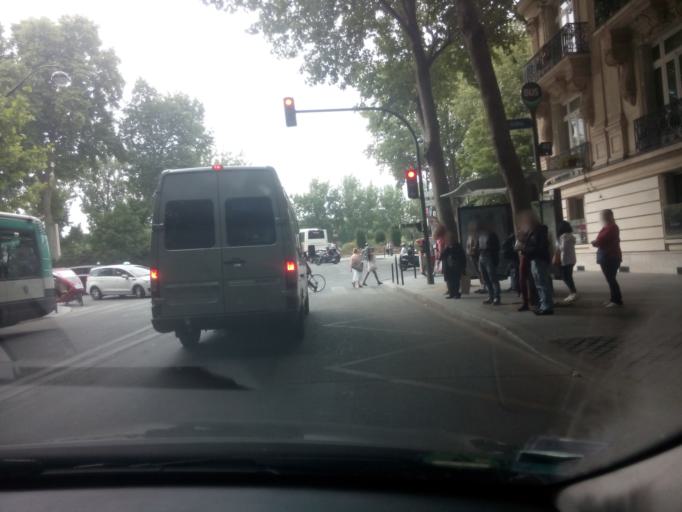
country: FR
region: Ile-de-France
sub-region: Departement des Hauts-de-Seine
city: Levallois-Perret
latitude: 48.8602
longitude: 2.2969
